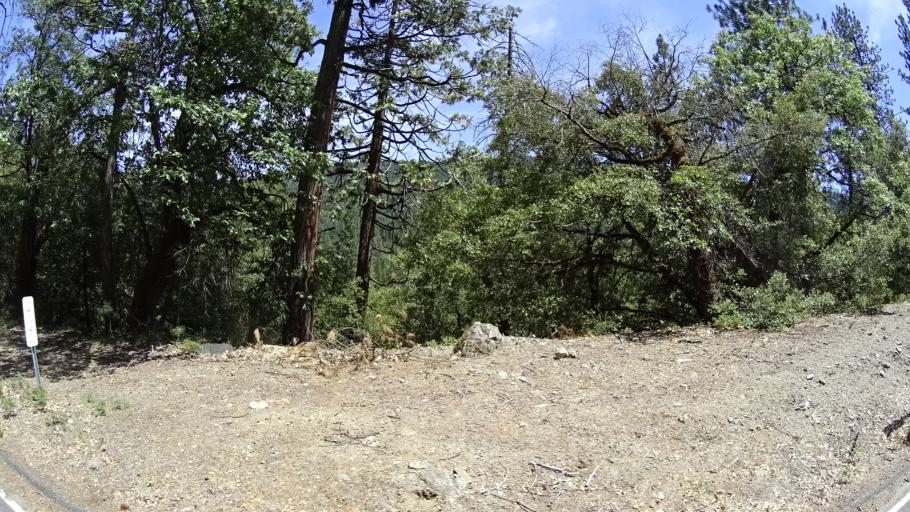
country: US
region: California
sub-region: Calaveras County
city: Arnold
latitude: 38.3191
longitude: -120.2265
